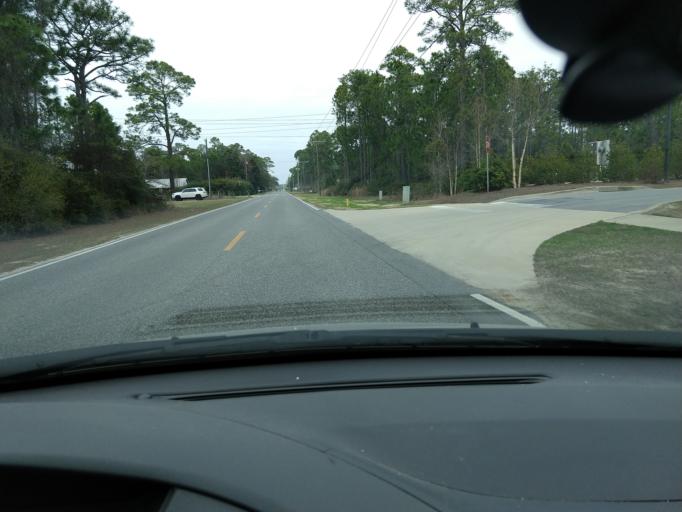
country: US
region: Florida
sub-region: Walton County
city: Miramar Beach
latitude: 30.3787
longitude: -86.2880
